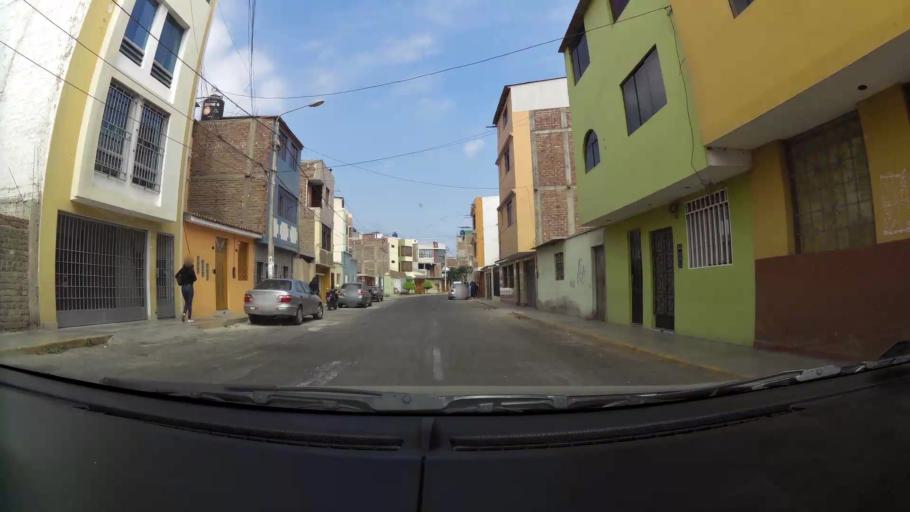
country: PE
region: La Libertad
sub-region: Provincia de Trujillo
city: Trujillo
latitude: -8.1182
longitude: -79.0234
